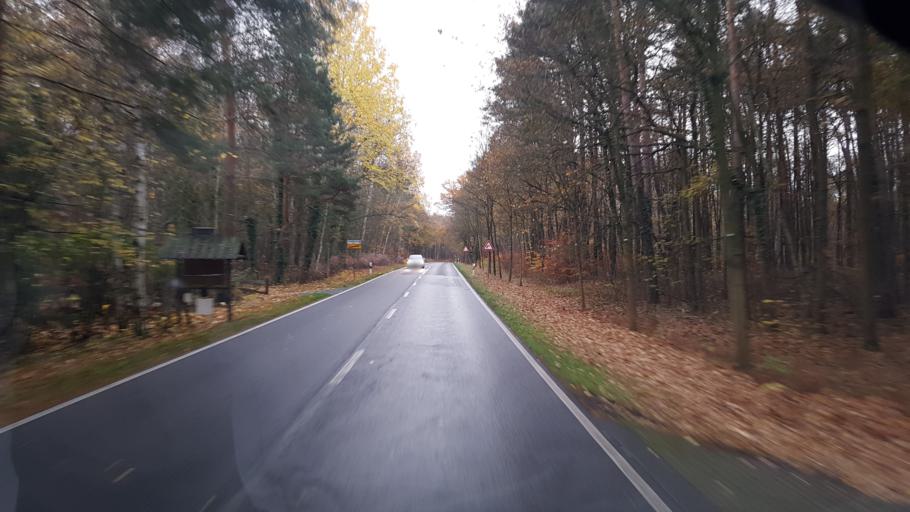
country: DE
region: Brandenburg
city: Lauchhammer
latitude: 51.5082
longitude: 13.7176
